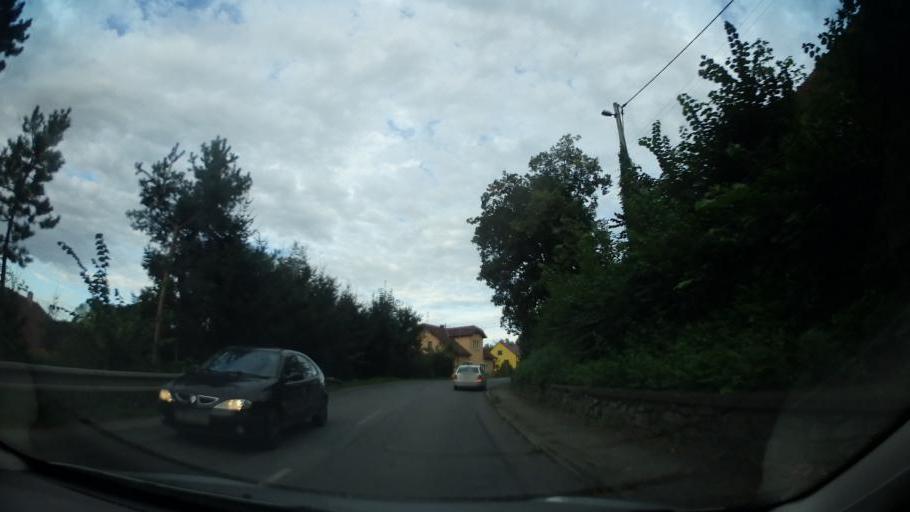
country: CZ
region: South Moravian
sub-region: Okres Blansko
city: Boskovice
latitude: 49.5396
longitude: 16.7002
